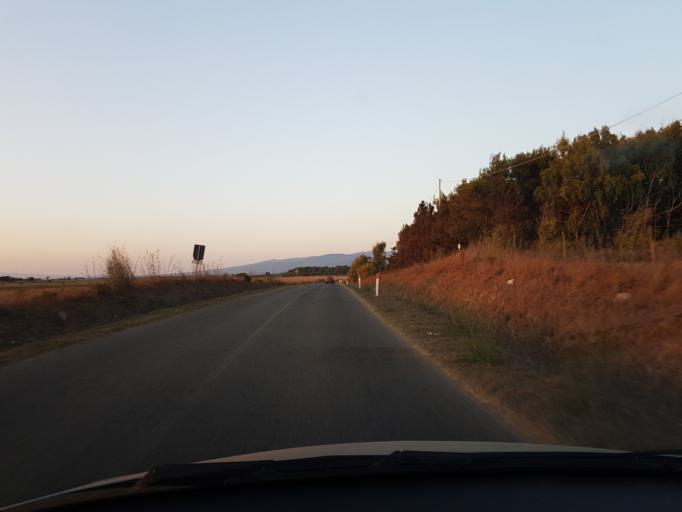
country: IT
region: Sardinia
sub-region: Provincia di Oristano
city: Nurachi
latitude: 39.9883
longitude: 8.4594
